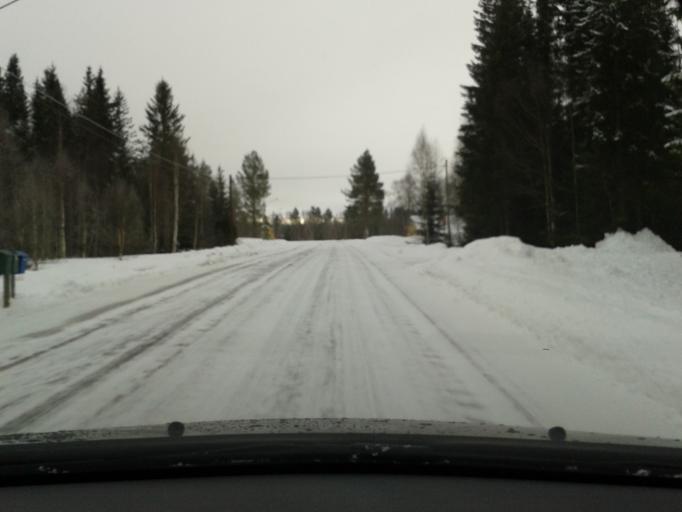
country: SE
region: Vaesterbotten
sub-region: Vilhelmina Kommun
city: Sjoberg
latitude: 64.8373
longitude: 15.9238
